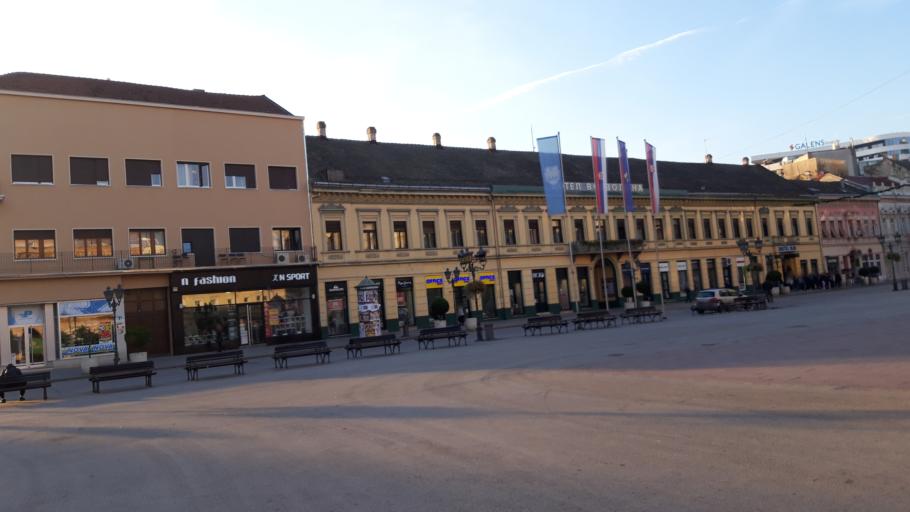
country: RS
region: Autonomna Pokrajina Vojvodina
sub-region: Juznobacki Okrug
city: Novi Sad
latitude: 45.2552
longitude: 19.8451
